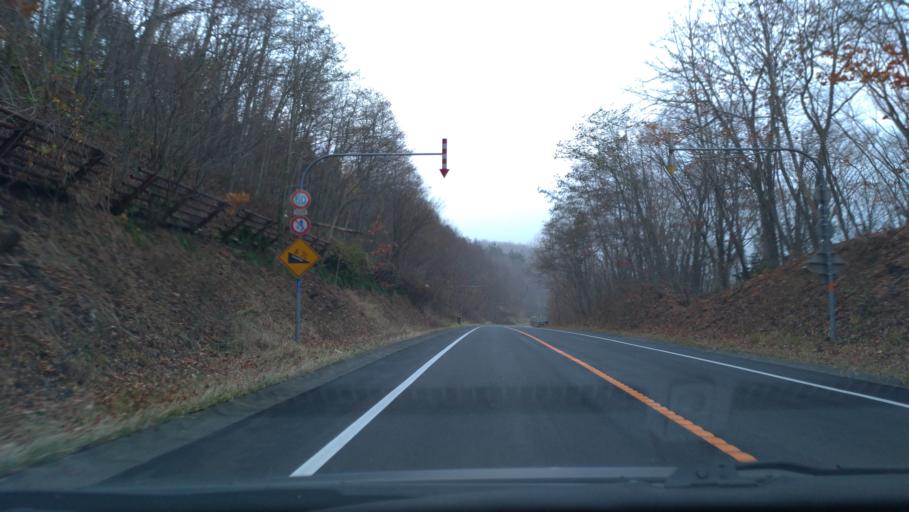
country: JP
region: Hokkaido
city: Shiraoi
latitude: 42.7447
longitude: 141.4112
